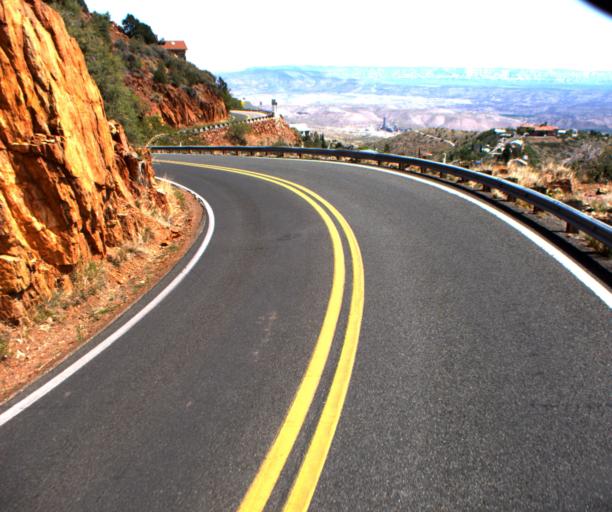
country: US
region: Arizona
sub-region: Yavapai County
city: Clarkdale
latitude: 34.7446
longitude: -112.1146
